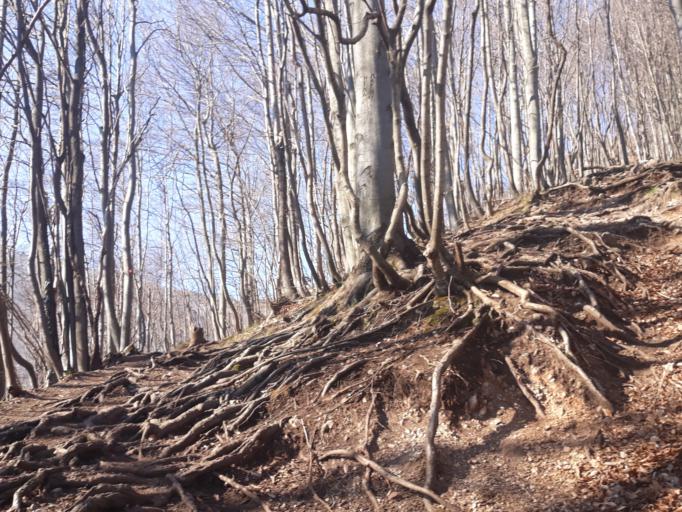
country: HR
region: Varazdinska
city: Ivanec
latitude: 46.1917
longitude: 16.1315
